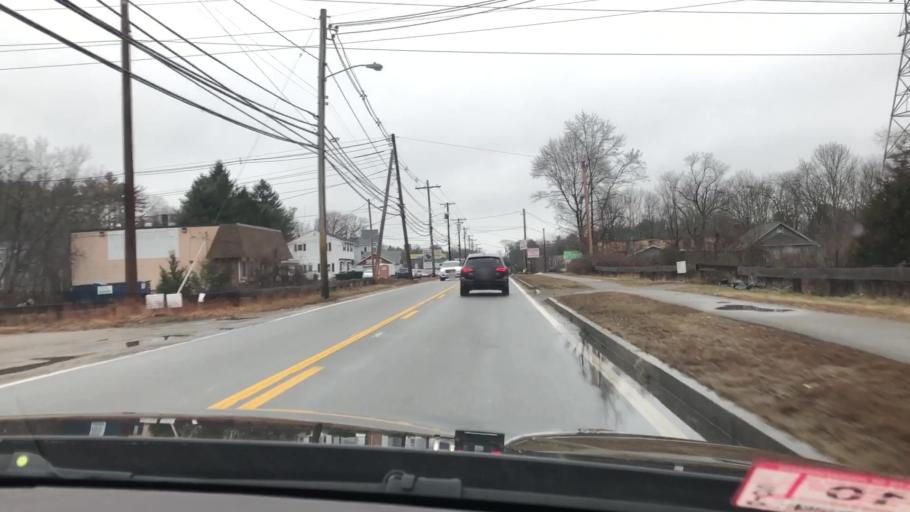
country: US
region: Massachusetts
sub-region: Norfolk County
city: Walpole
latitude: 42.1308
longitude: -71.2637
